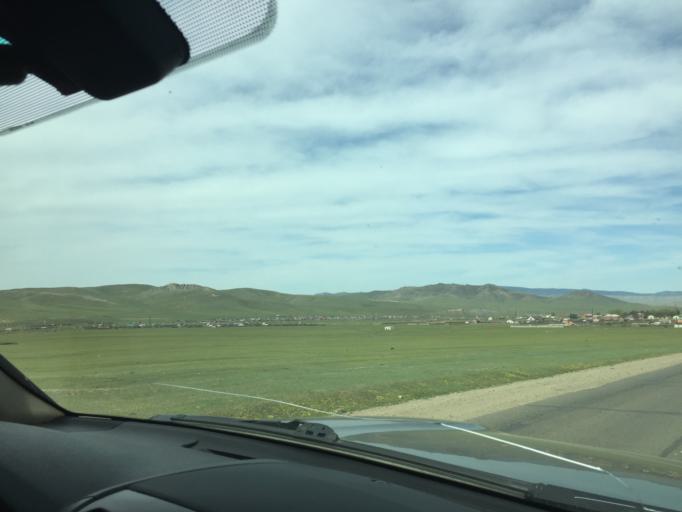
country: MN
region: Central Aimak
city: Ihsueuej
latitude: 48.2169
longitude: 106.3062
